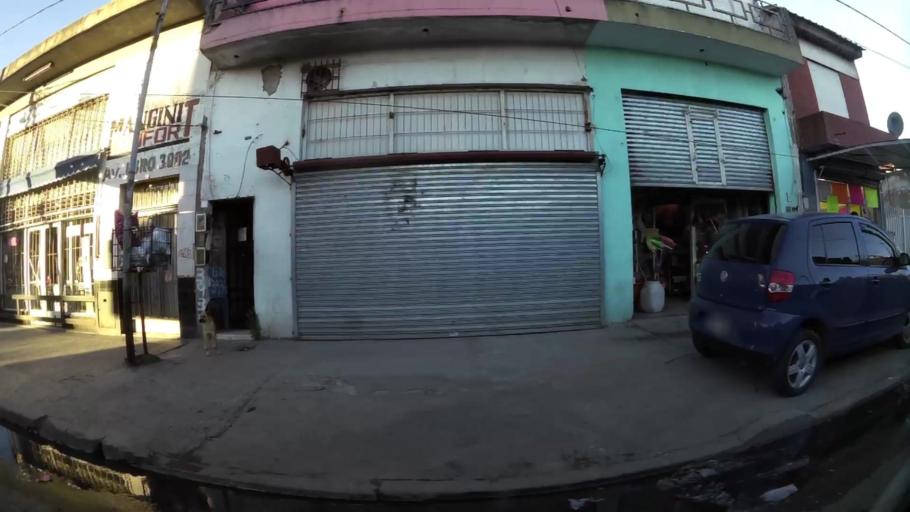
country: AR
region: Buenos Aires
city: San Justo
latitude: -34.7328
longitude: -58.6076
